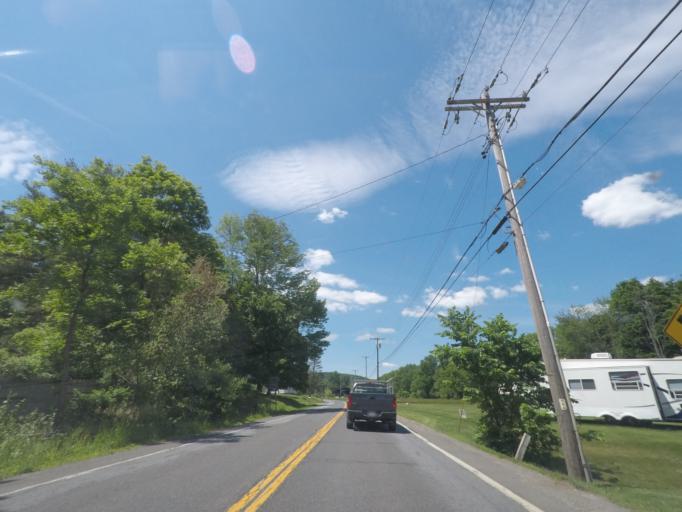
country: US
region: New York
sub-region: Dutchess County
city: Pine Plains
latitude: 41.9597
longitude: -73.5182
